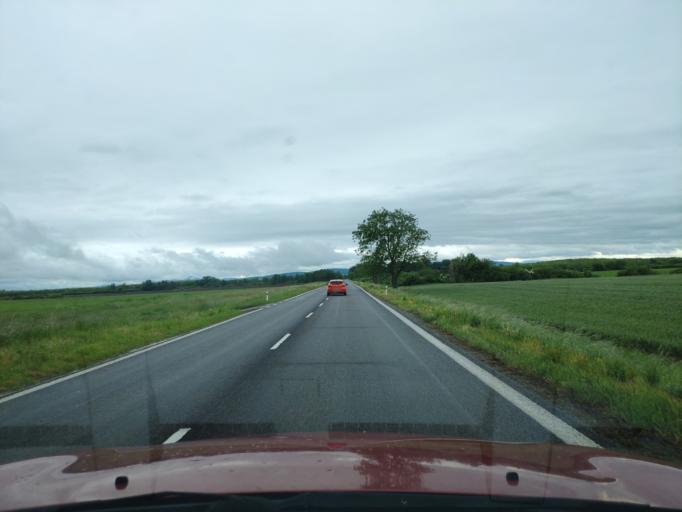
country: HU
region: Borsod-Abauj-Zemplen
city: Ricse
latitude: 48.4326
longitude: 21.9016
